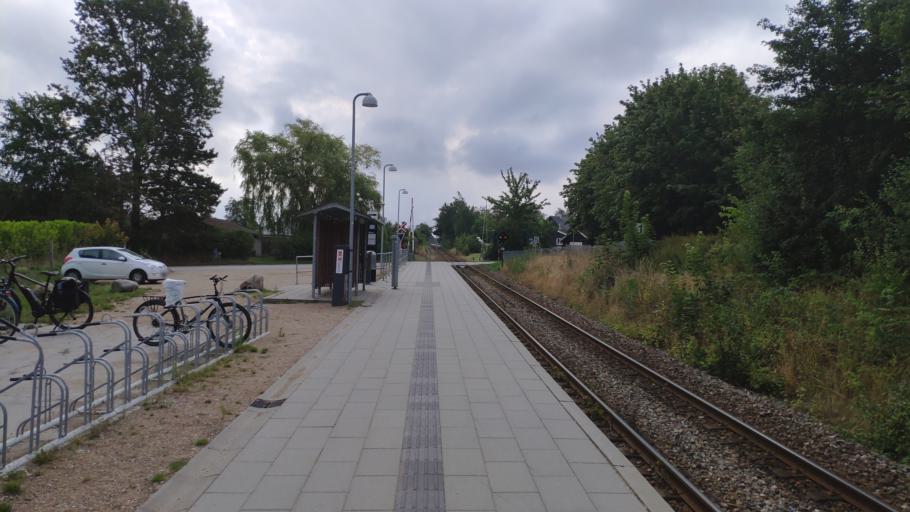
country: DK
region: Capital Region
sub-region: Halsnaes Kommune
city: Frederiksvaerk
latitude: 55.9467
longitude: 12.0341
